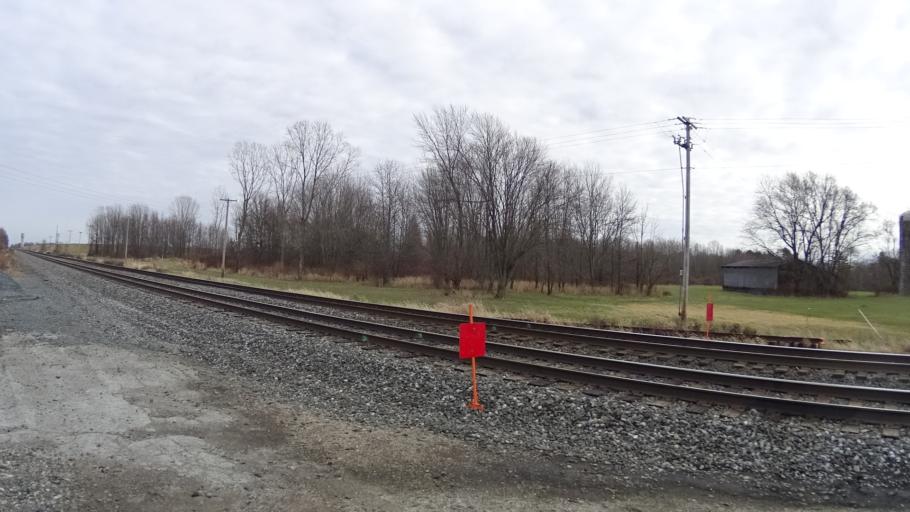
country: US
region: Ohio
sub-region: Lorain County
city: Wellington
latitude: 41.1532
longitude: -82.2435
